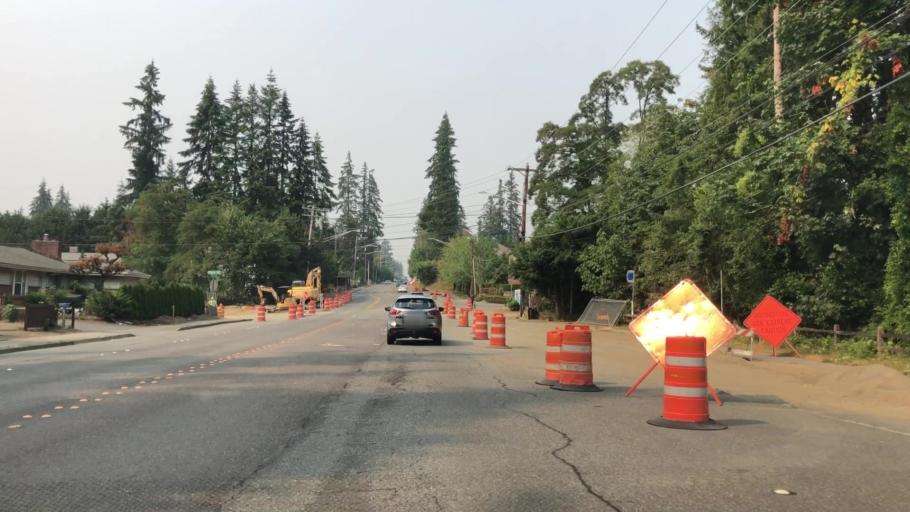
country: US
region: Washington
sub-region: Snohomish County
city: Alderwood Manor
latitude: 47.8356
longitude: -122.2817
